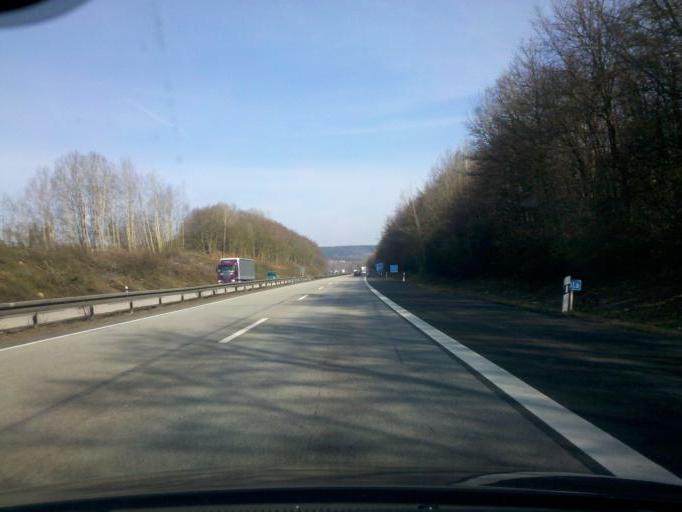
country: DE
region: North Rhine-Westphalia
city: Freudenberg
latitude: 50.9005
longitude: 7.9192
